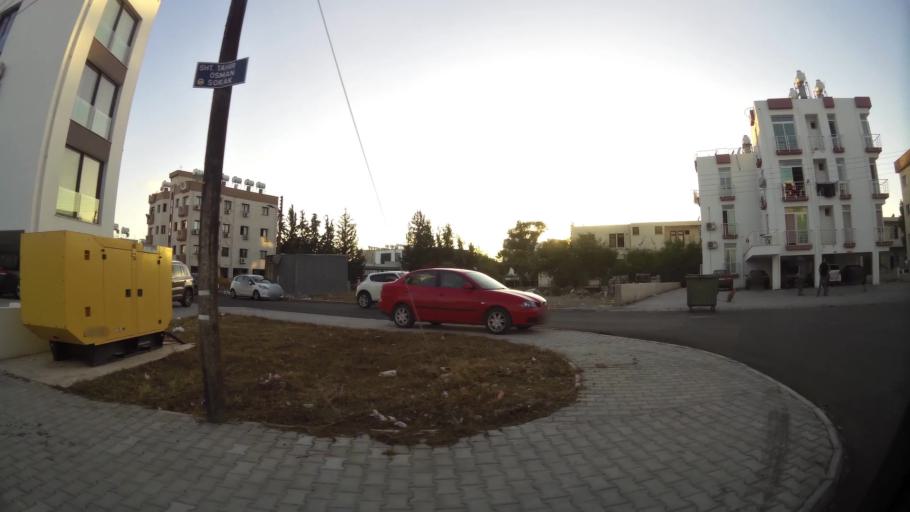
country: CY
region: Lefkosia
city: Nicosia
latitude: 35.2057
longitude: 33.3318
